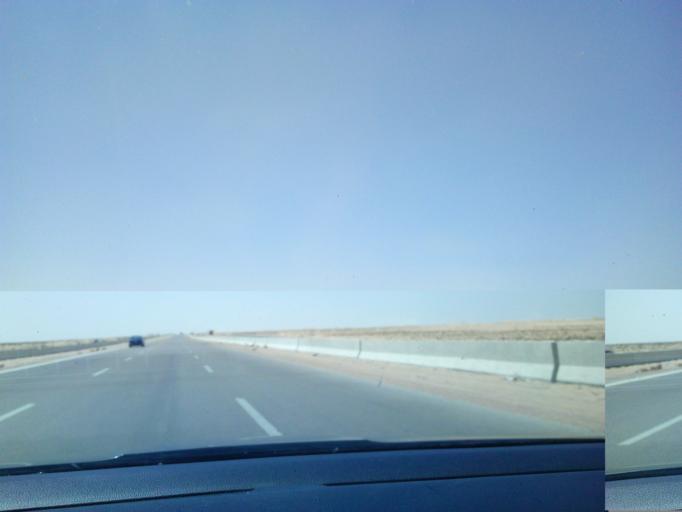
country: EG
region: Al Buhayrah
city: Abu al Matamir
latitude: 30.6368
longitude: 29.7490
